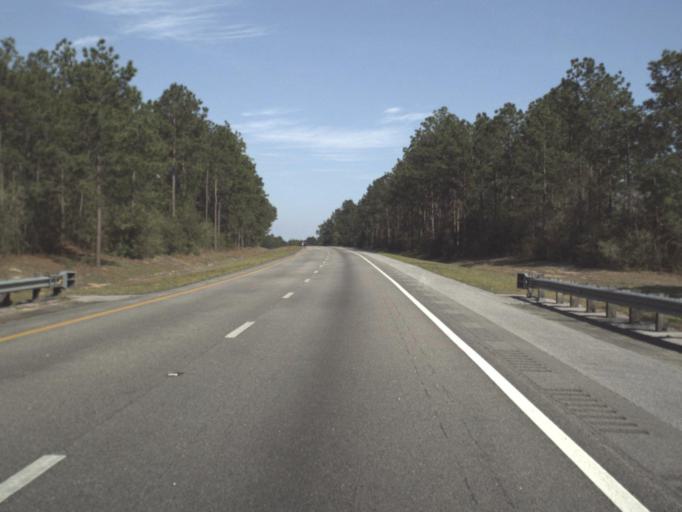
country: US
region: Florida
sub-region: Okaloosa County
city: Crestview
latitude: 30.7219
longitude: -86.4841
